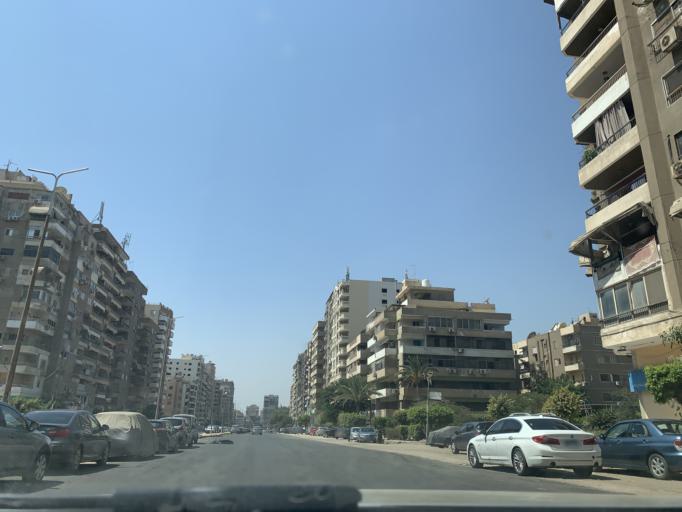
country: EG
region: Muhafazat al Qahirah
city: Cairo
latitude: 30.0614
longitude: 31.3541
